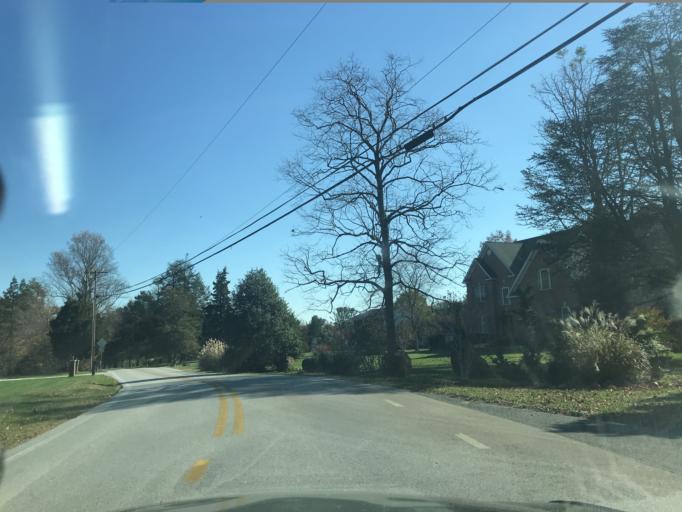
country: US
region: Maryland
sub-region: Baltimore County
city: Kingsville
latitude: 39.4276
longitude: -76.4162
